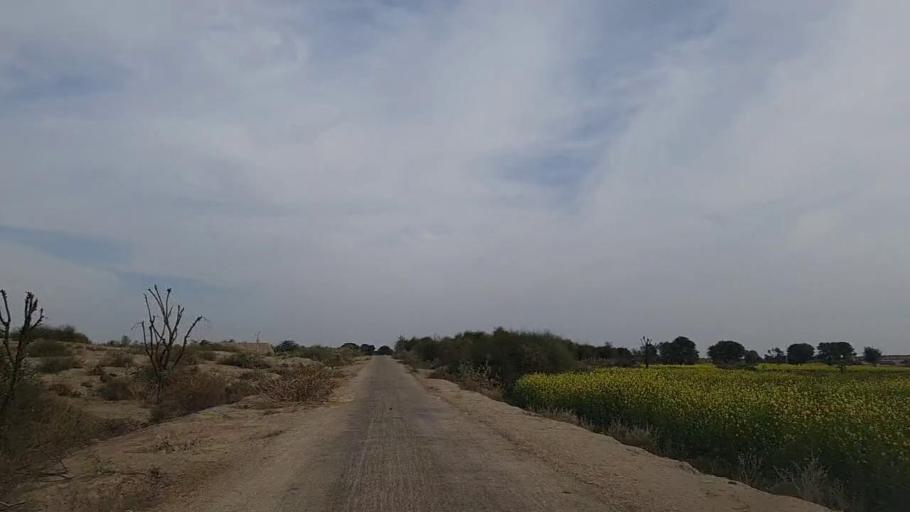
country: PK
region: Sindh
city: Jam Sahib
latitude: 26.4415
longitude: 68.5989
